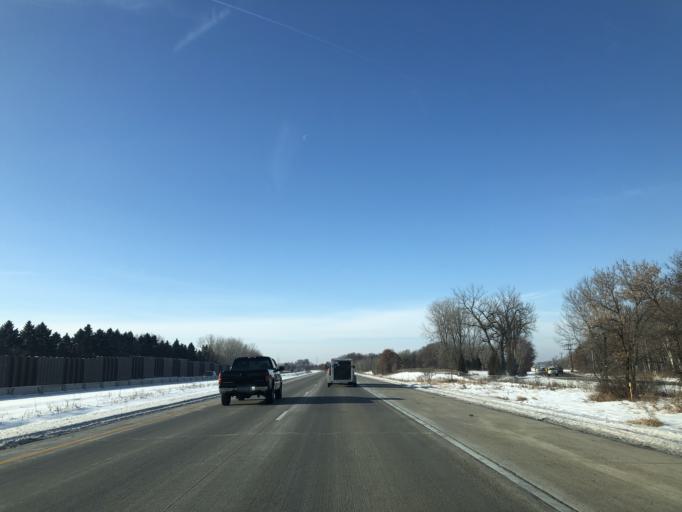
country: US
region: Minnesota
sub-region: Anoka County
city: Circle Pines
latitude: 45.1675
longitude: -93.1464
